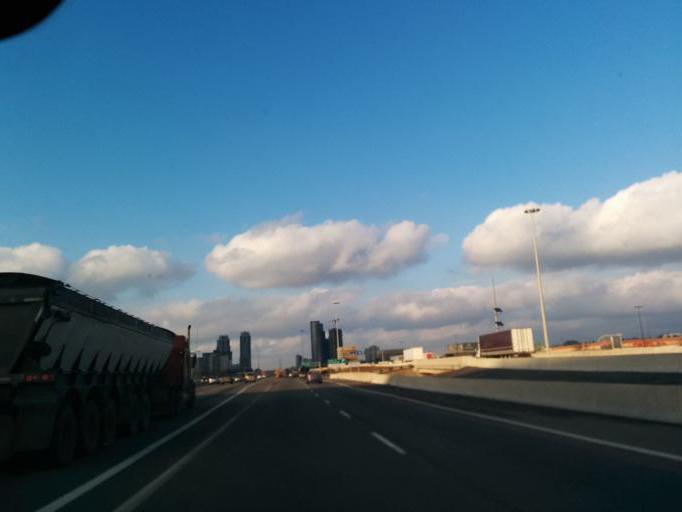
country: CA
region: Ontario
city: Etobicoke
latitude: 43.6277
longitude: -79.5562
